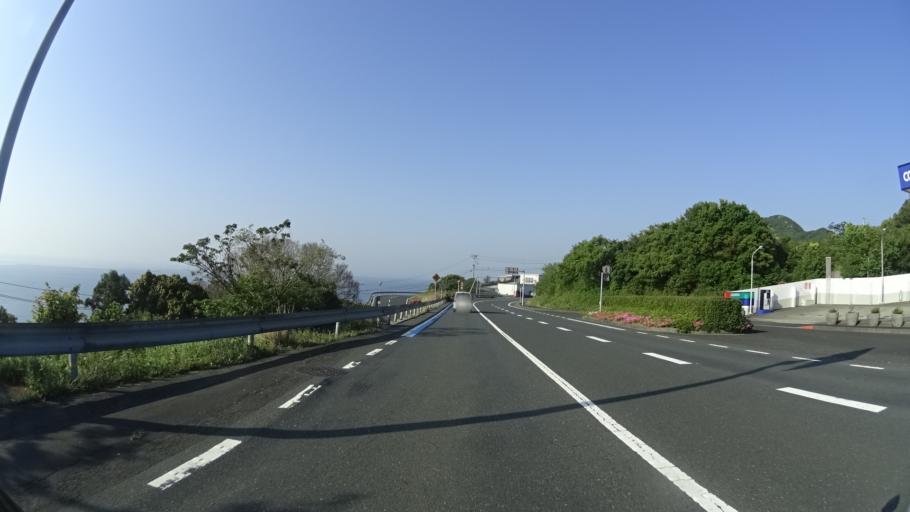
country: JP
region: Ehime
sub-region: Nishiuwa-gun
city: Ikata-cho
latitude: 33.4053
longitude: 132.1717
